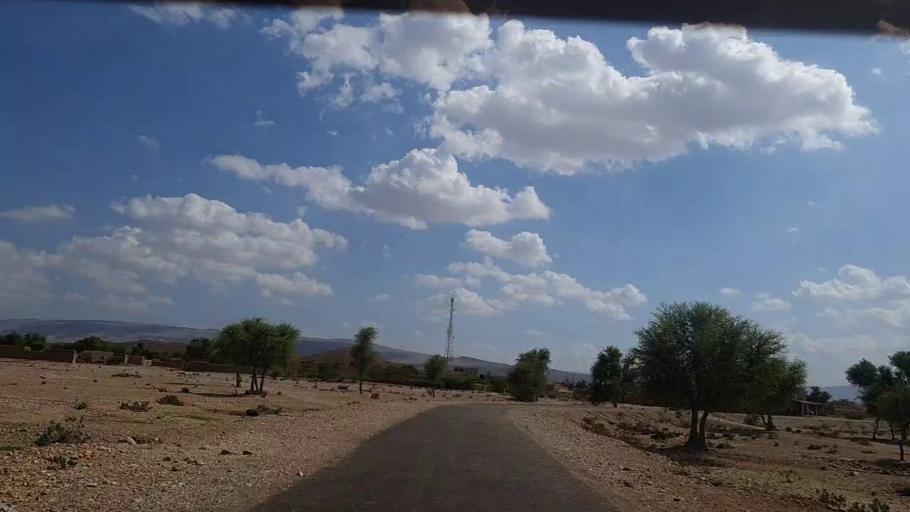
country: PK
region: Sindh
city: Johi
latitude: 26.4998
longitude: 67.4352
